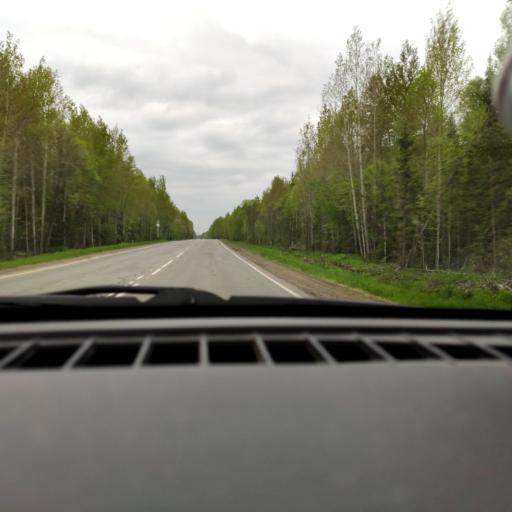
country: RU
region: Perm
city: Polazna
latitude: 58.2665
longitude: 56.1678
